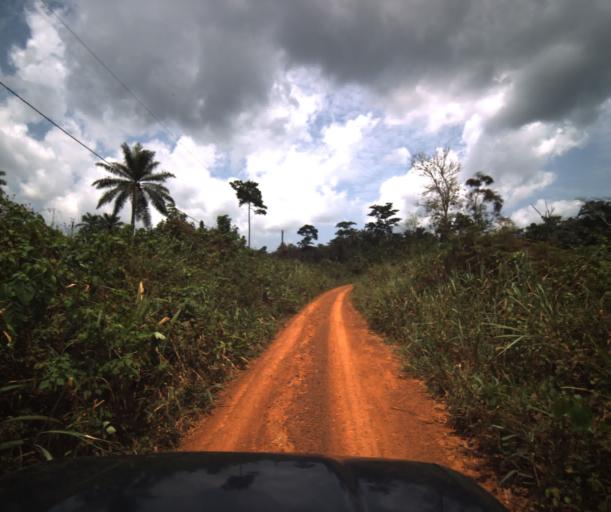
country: CM
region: Centre
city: Eseka
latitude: 3.5509
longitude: 10.9216
